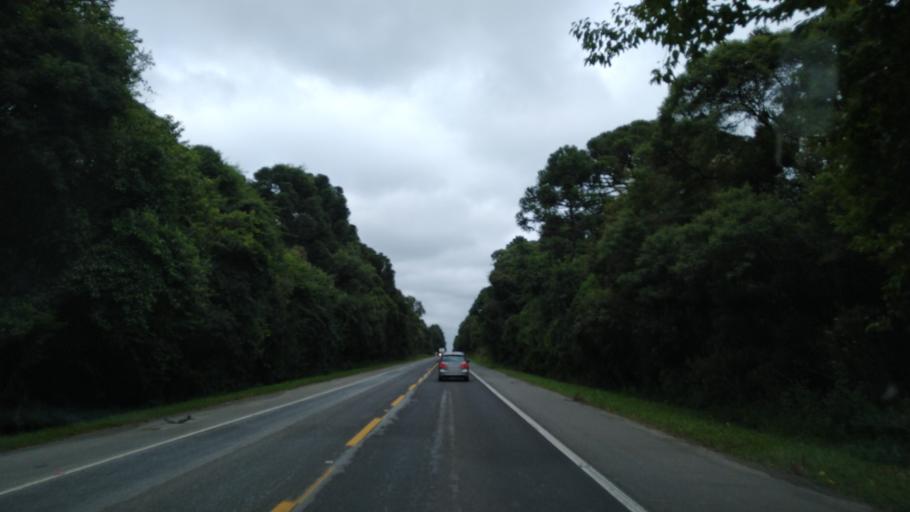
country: BR
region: Santa Catarina
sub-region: Tres Barras
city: Tres Barras
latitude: -26.1650
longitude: -50.1151
